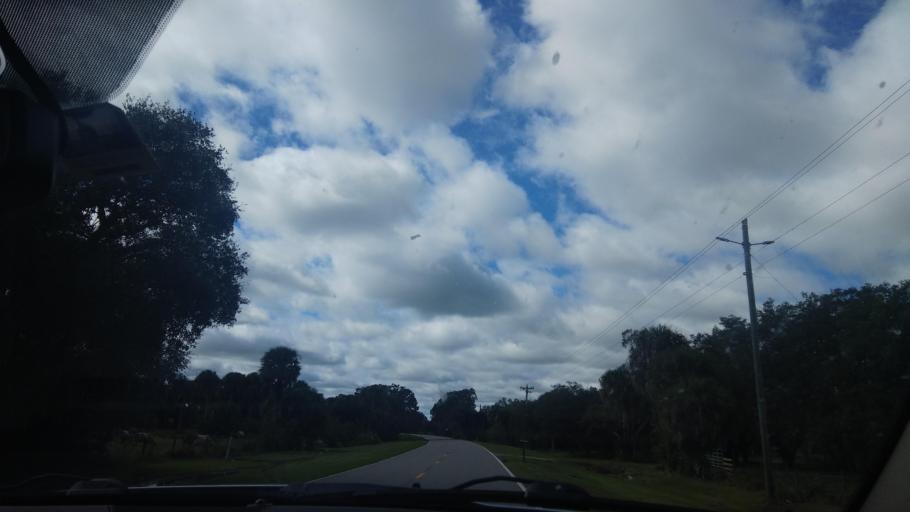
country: US
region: Florida
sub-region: Okeechobee County
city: Okeechobee
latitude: 27.3951
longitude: -80.9129
